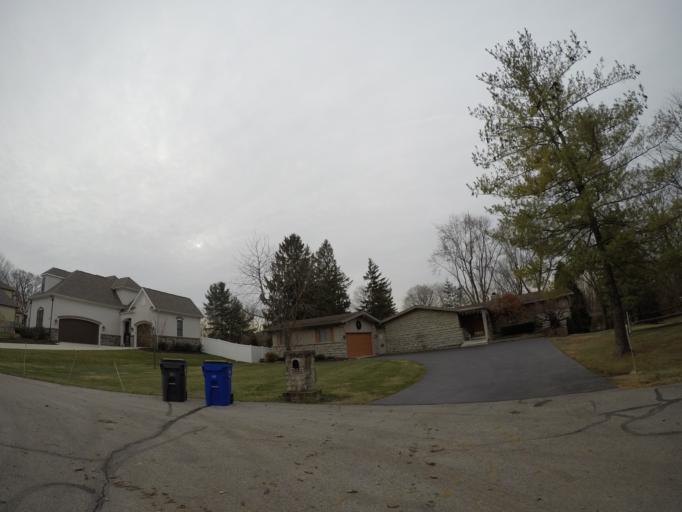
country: US
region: Ohio
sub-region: Franklin County
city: Dublin
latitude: 40.0587
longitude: -83.0952
